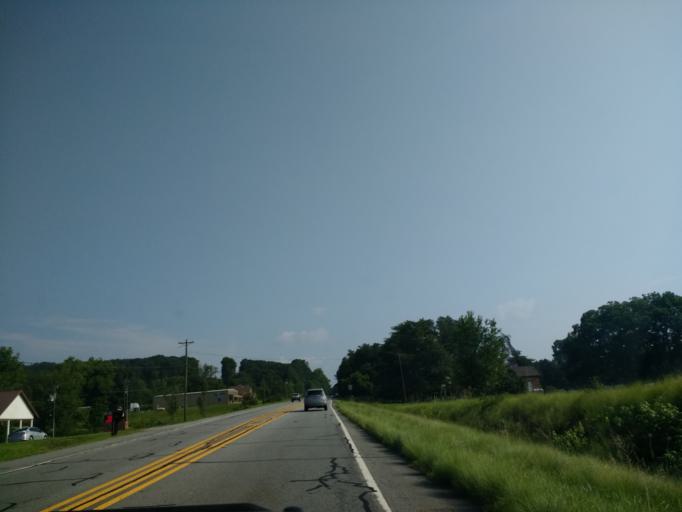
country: US
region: Georgia
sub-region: White County
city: Cleveland
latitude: 34.5197
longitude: -83.7550
